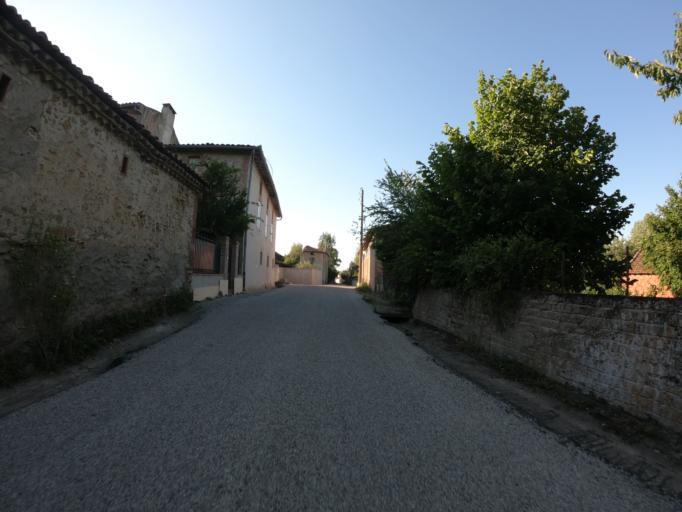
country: FR
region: Midi-Pyrenees
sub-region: Departement de l'Ariege
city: La Tour-du-Crieu
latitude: 43.1101
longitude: 1.7254
